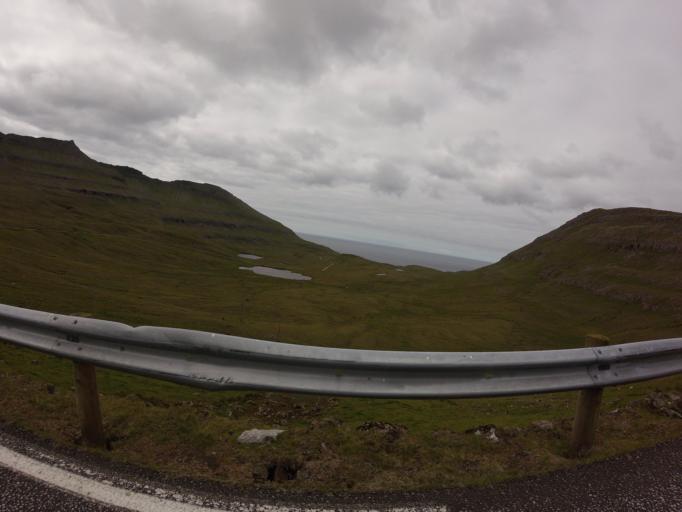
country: FO
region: Suduroy
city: Tvoroyri
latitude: 61.5198
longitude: -6.8368
